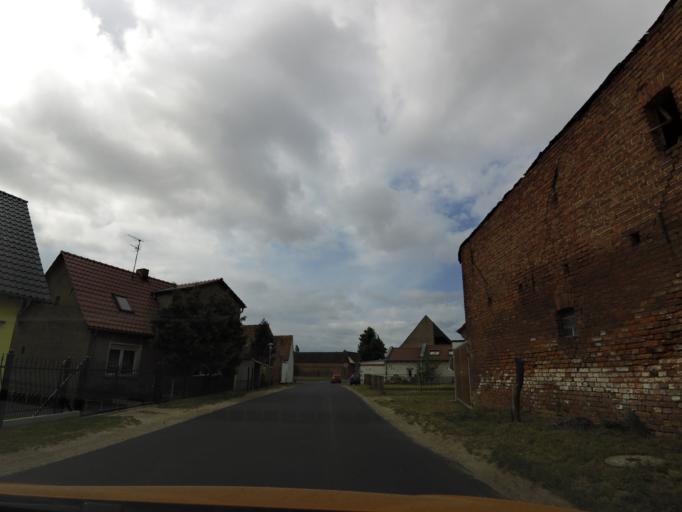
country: DE
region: Brandenburg
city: Niemegk
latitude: 52.1037
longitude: 12.6728
